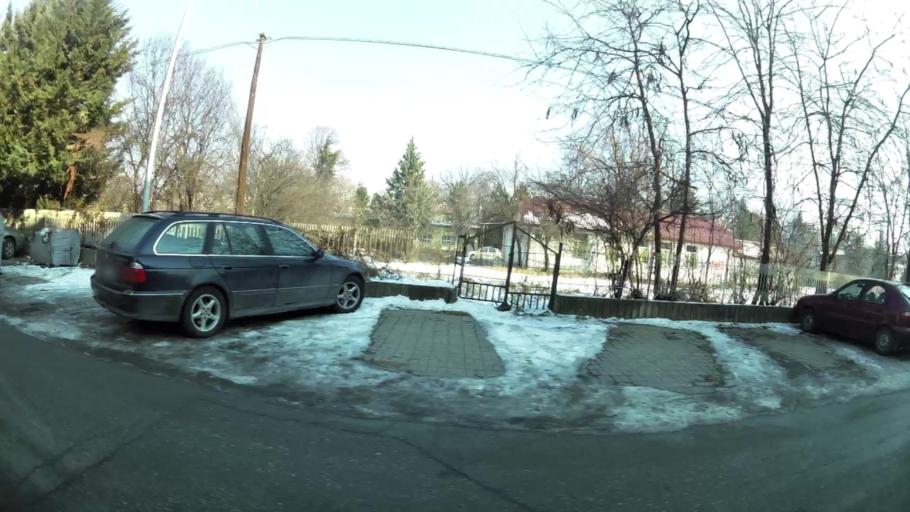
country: MK
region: Karpos
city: Skopje
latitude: 41.9756
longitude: 21.4403
